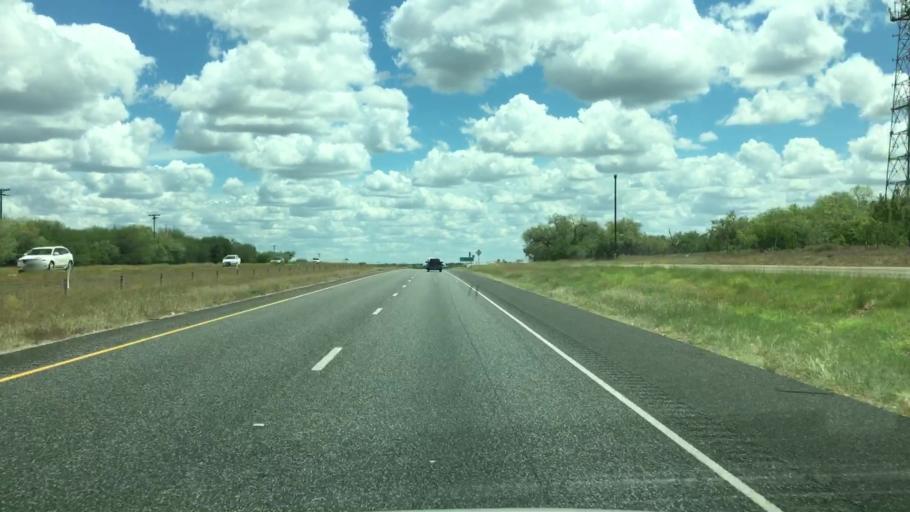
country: US
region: Texas
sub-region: Atascosa County
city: Pleasanton
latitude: 28.9014
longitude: -98.4227
